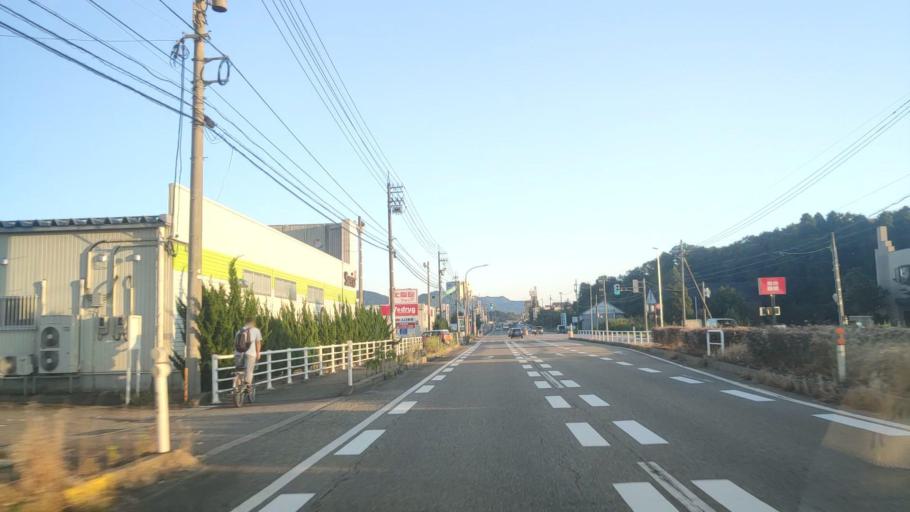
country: JP
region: Toyama
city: Himi
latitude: 36.8328
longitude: 136.9913
